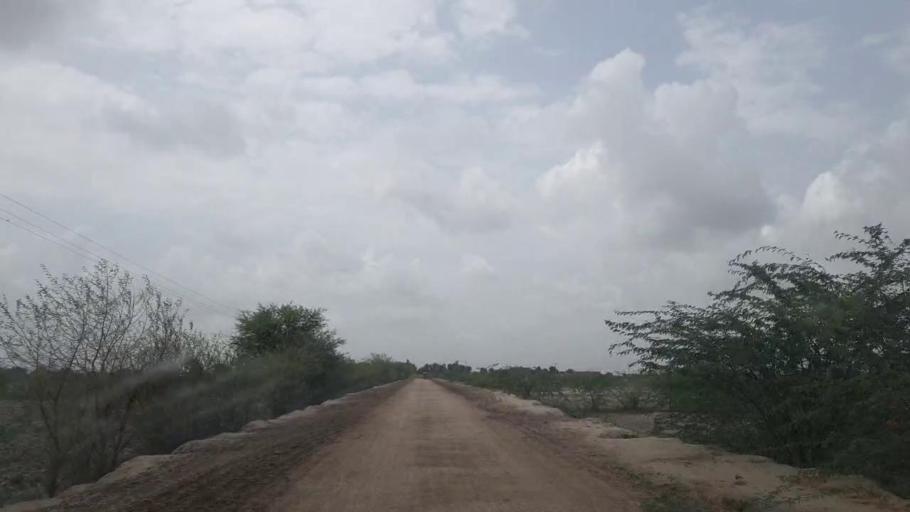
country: PK
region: Sindh
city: Naukot
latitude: 24.9453
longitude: 69.2586
